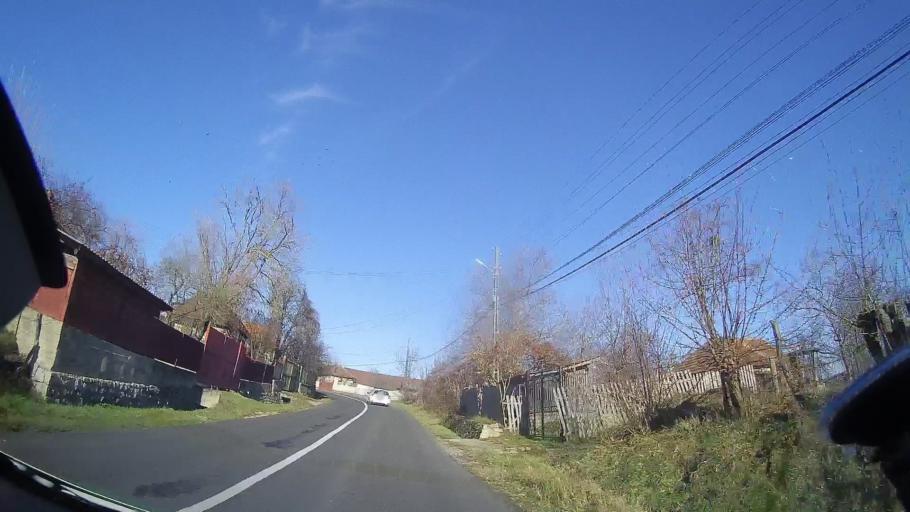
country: RO
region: Bihor
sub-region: Comuna Bratca
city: Beznea
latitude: 46.9631
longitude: 22.6172
